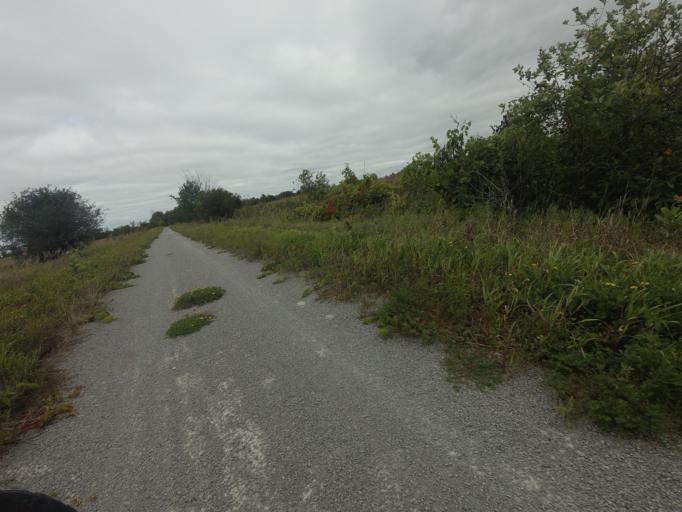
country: CA
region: Ontario
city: Uxbridge
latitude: 44.3068
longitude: -78.8971
